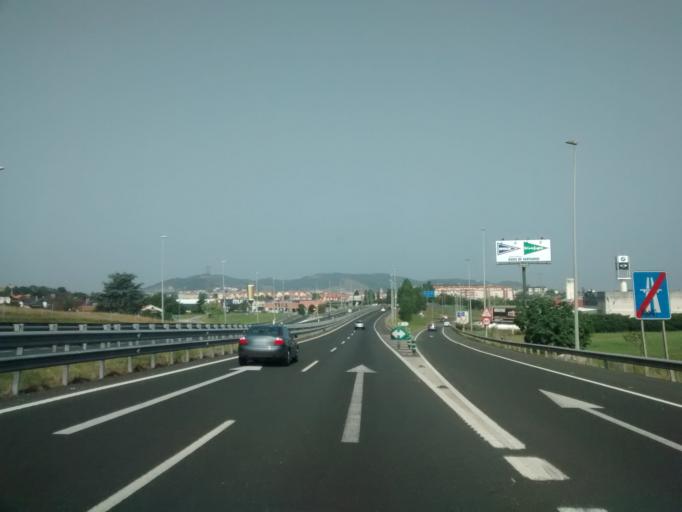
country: ES
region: Cantabria
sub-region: Provincia de Cantabria
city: Santa Cruz de Bezana
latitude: 43.4386
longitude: -3.8849
